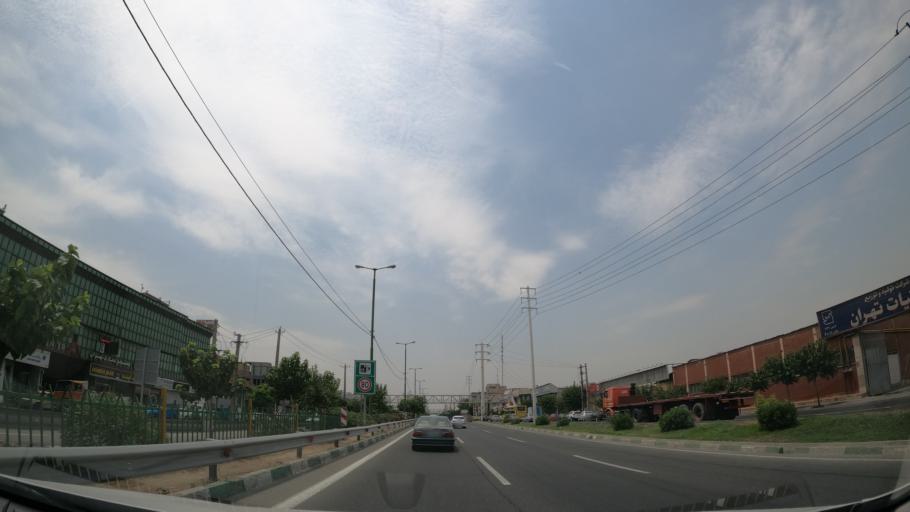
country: IR
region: Tehran
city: Tehran
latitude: 35.6760
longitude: 51.3030
